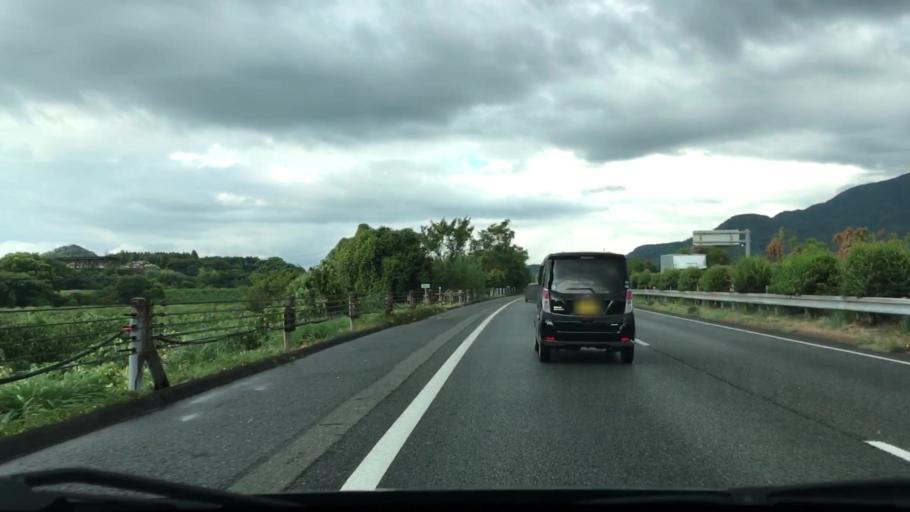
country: JP
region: Fukuoka
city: Koga
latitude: 33.7324
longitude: 130.5095
